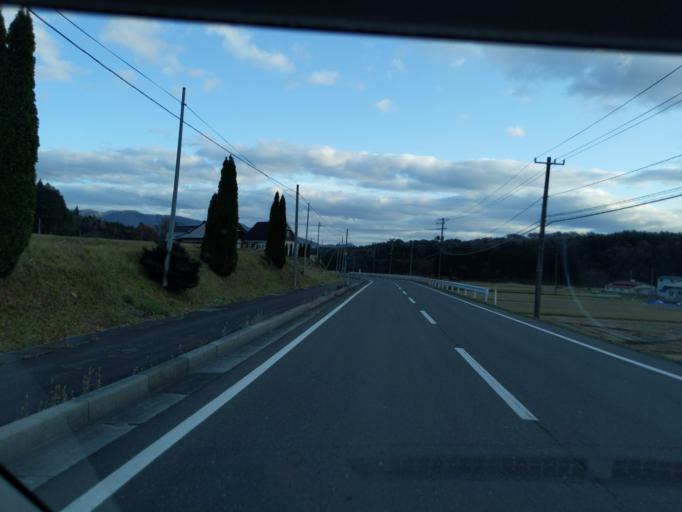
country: JP
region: Iwate
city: Mizusawa
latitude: 39.0483
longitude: 141.0967
